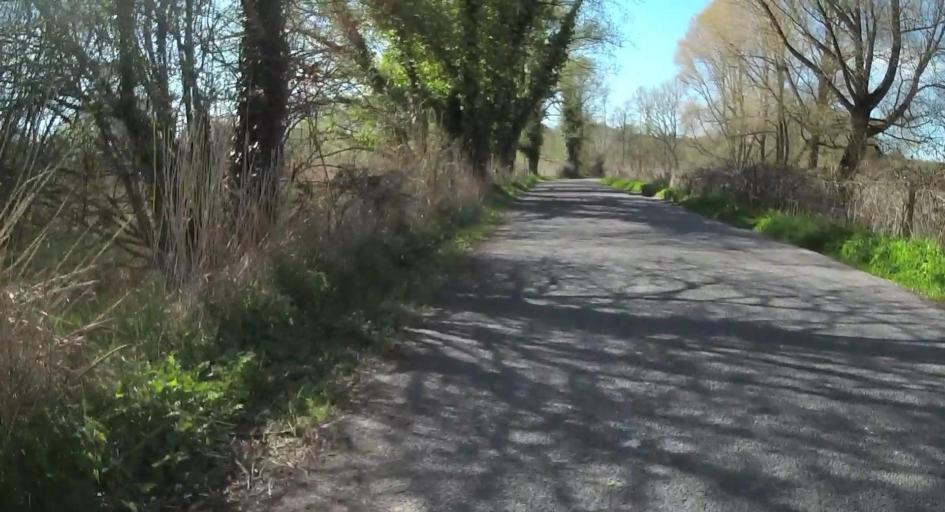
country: GB
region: England
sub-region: Hampshire
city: Abbotts Ann
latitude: 51.1294
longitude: -1.4839
